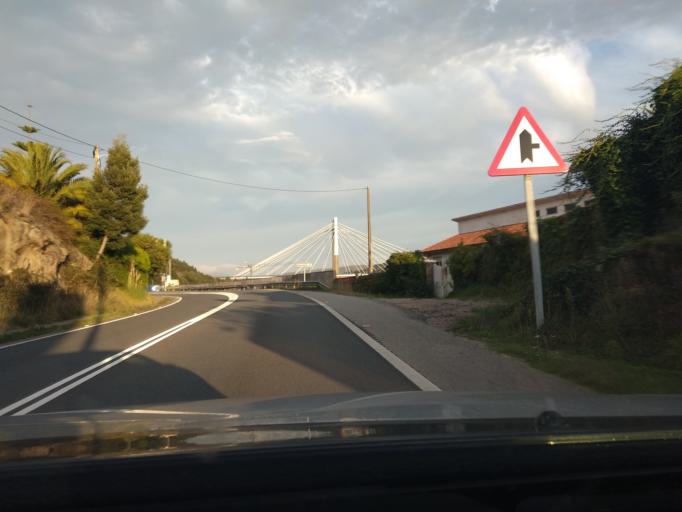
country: ES
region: Galicia
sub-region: Provincia de Pontevedra
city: Redondela
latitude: 42.2914
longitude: -8.6694
